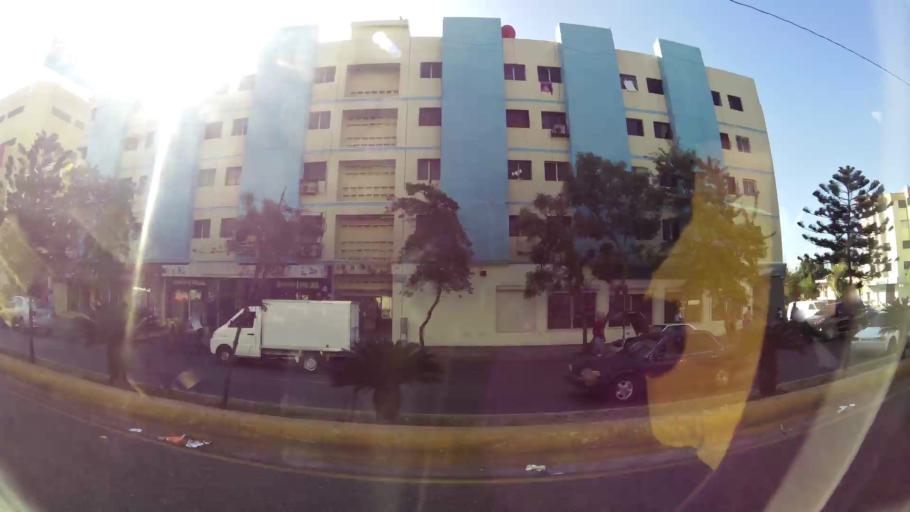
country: DO
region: Nacional
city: San Carlos
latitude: 18.4789
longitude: -69.8895
